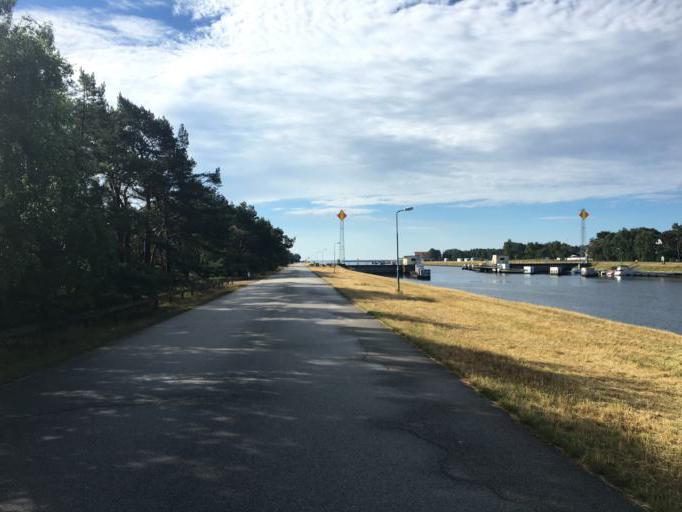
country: SE
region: Skane
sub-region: Vellinge Kommun
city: Hollviken
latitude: 55.4031
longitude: 12.9415
